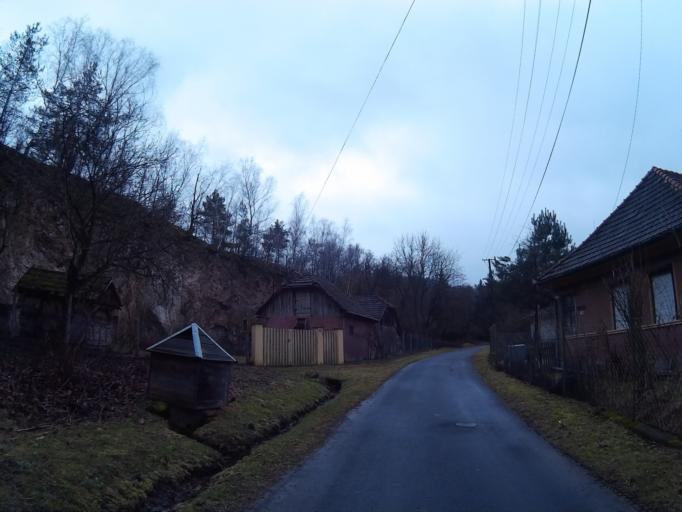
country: HU
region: Borsod-Abauj-Zemplen
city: Sarospatak
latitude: 48.4729
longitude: 21.4694
